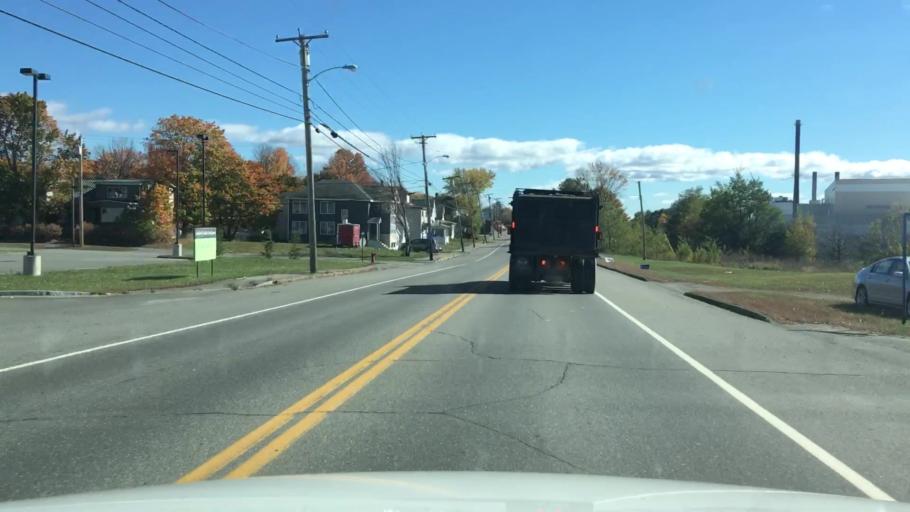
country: US
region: Maine
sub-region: Penobscot County
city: East Millinocket
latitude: 45.6272
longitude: -68.5814
